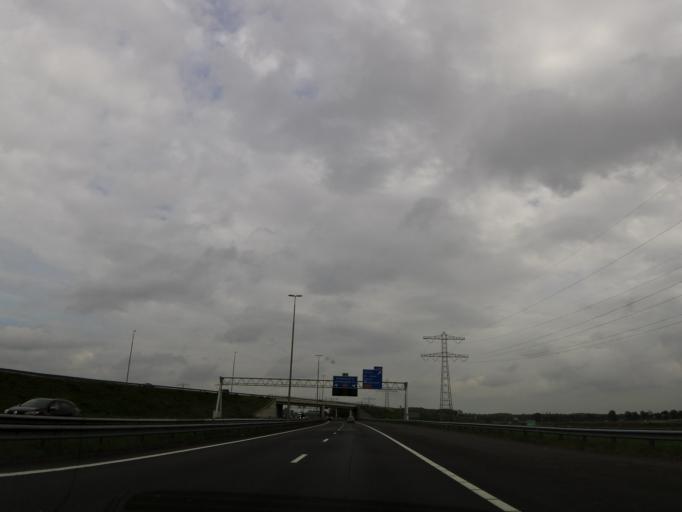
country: NL
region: Limburg
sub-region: Gemeente Maasgouw
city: Maasbracht
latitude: 51.1246
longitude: 5.8872
